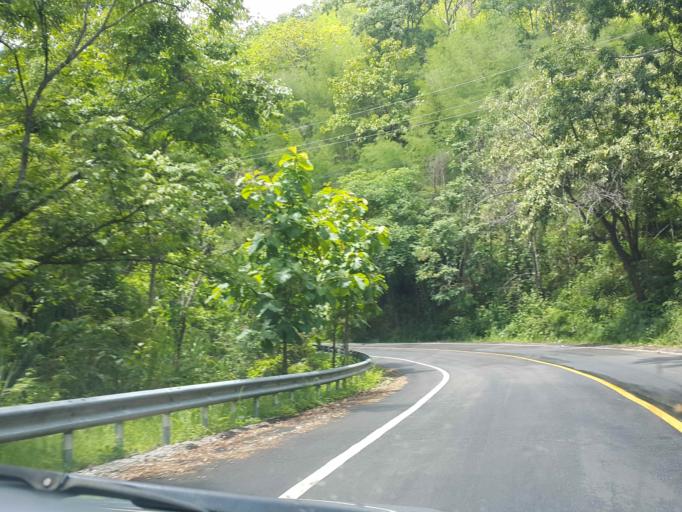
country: TH
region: Chiang Mai
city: Samoeng
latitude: 18.8473
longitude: 98.7723
